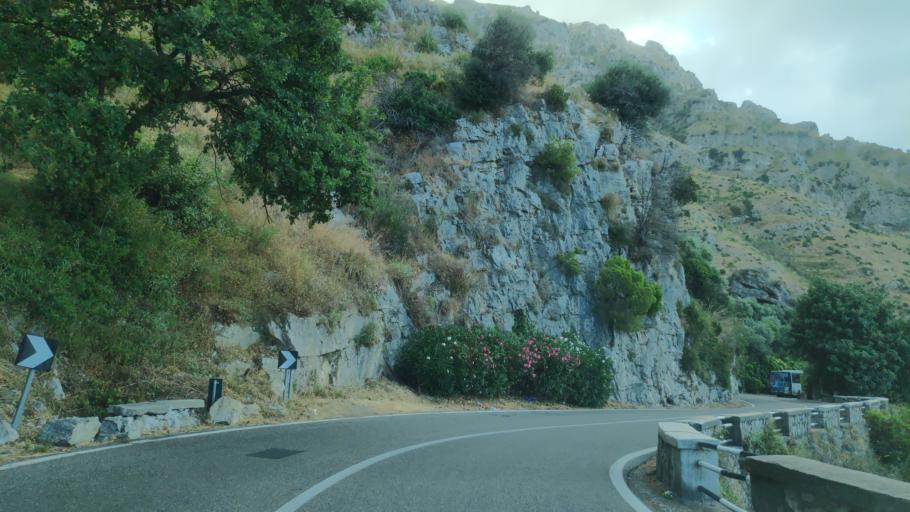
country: IT
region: Campania
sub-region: Provincia di Napoli
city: Arola-Preazzano
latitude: 40.6207
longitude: 14.4513
